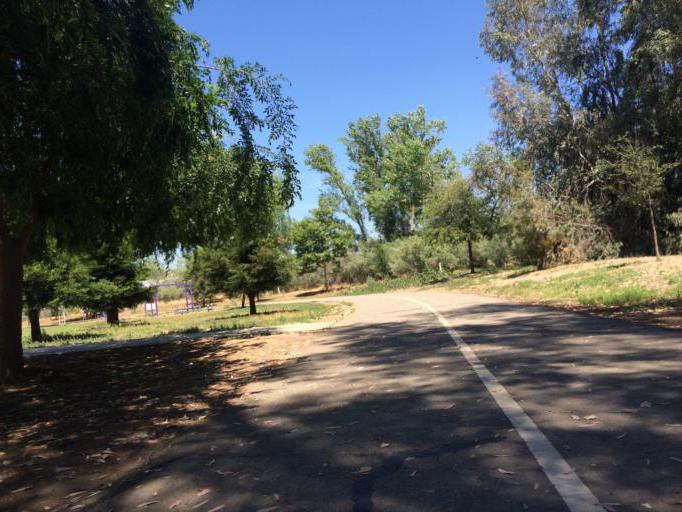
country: US
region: California
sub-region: Fresno County
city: Clovis
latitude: 36.8468
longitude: -119.7000
